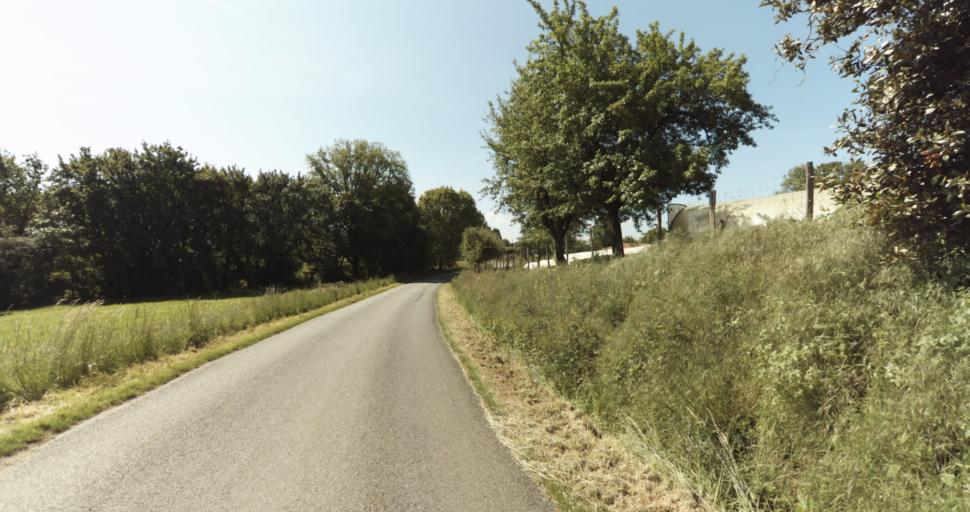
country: FR
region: Limousin
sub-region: Departement de la Haute-Vienne
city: Le Vigen
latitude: 45.7147
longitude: 1.2905
